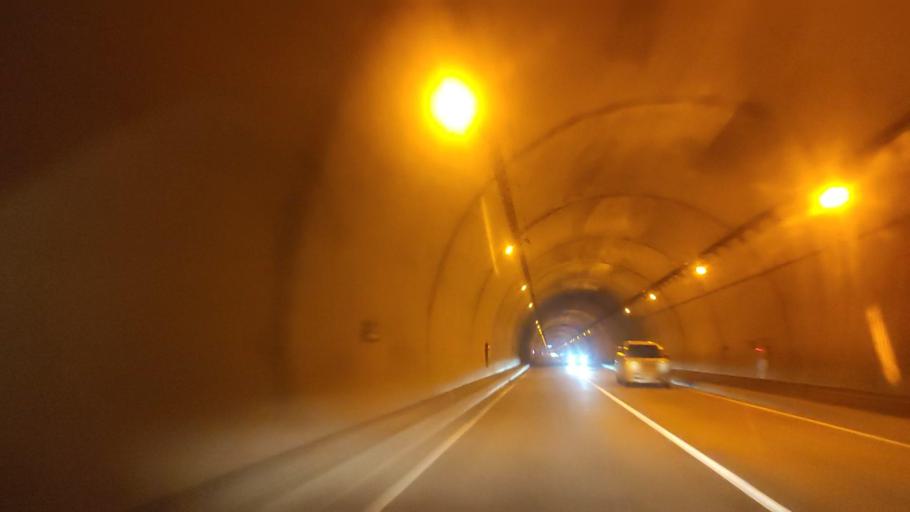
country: JP
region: Hokkaido
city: Date
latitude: 42.5639
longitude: 140.7860
